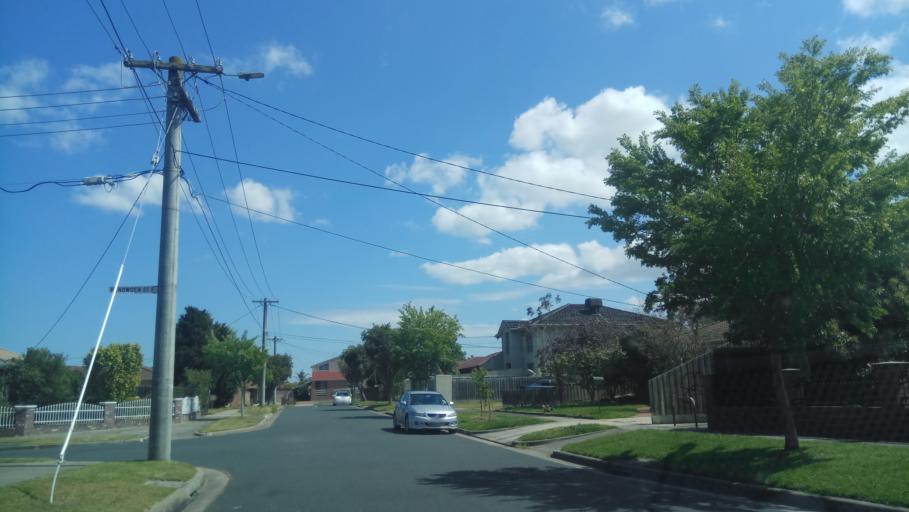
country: AU
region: Victoria
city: Heatherton
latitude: -37.9652
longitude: 145.0855
